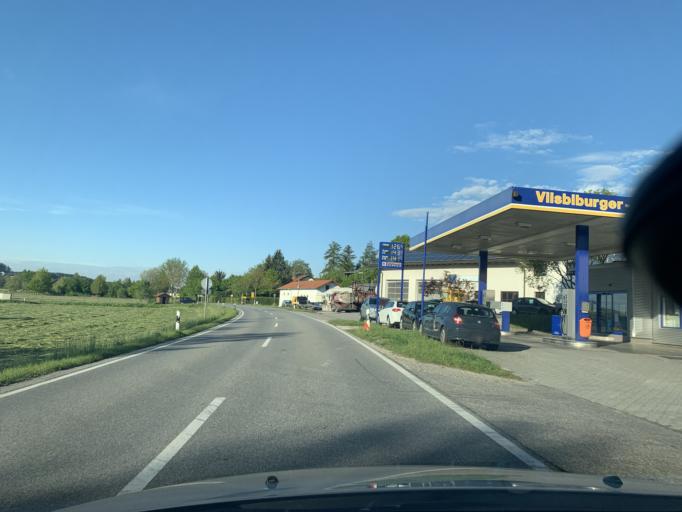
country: DE
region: Bavaria
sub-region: Lower Bavaria
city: Schalkham
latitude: 48.4769
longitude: 12.3852
